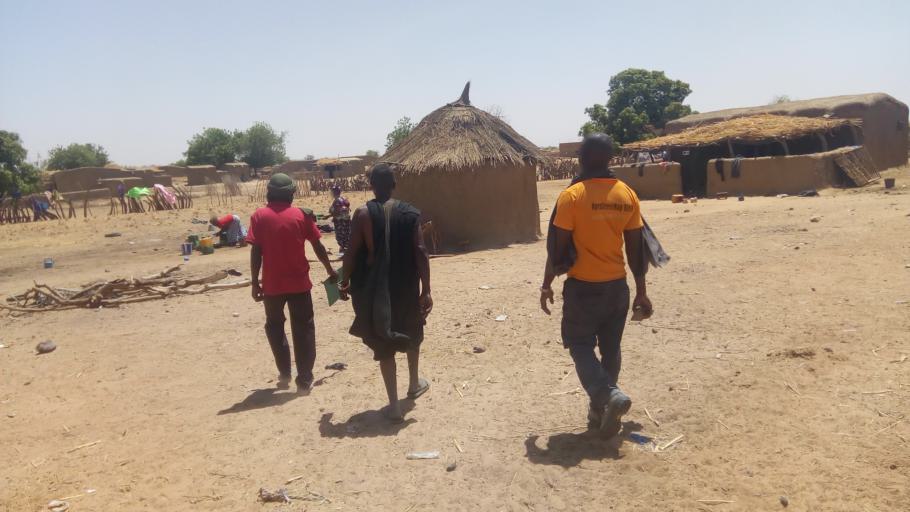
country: ML
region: Kayes
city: Diema
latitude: 14.5105
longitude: -8.8409
